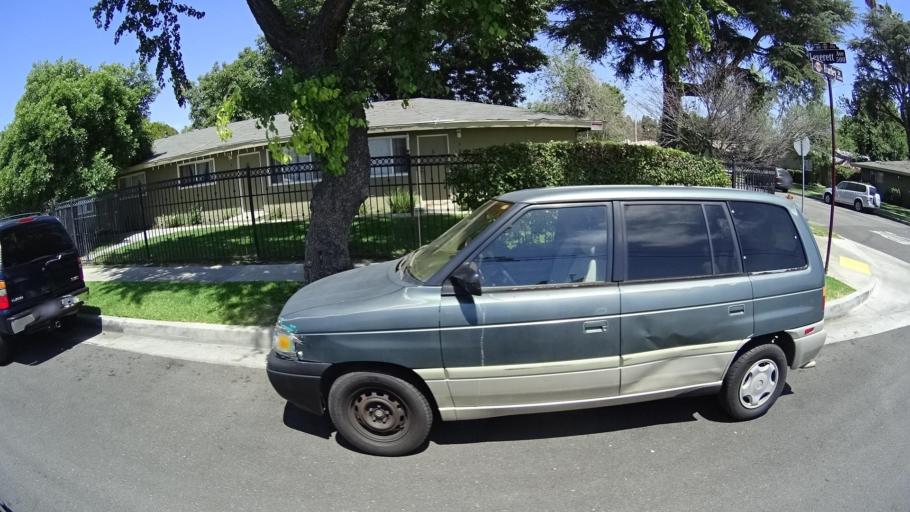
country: US
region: California
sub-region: Los Angeles County
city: South San Jose Hills
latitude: 34.0118
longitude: -117.9267
